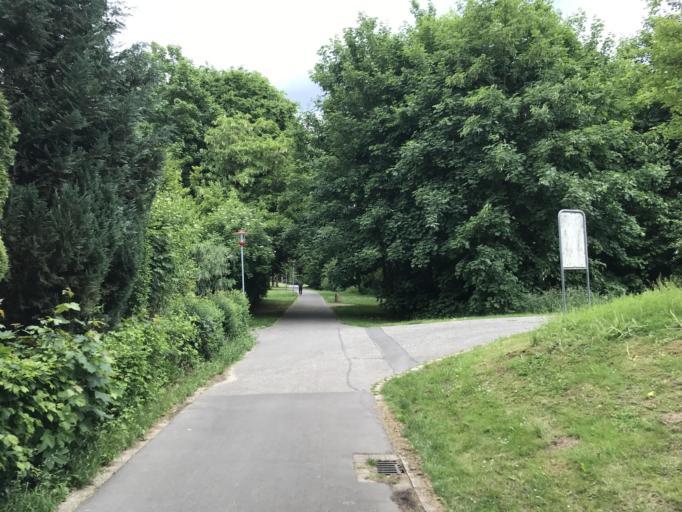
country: DE
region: Hesse
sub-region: Regierungsbezirk Kassel
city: Baunatal
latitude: 51.2468
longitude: 9.4078
